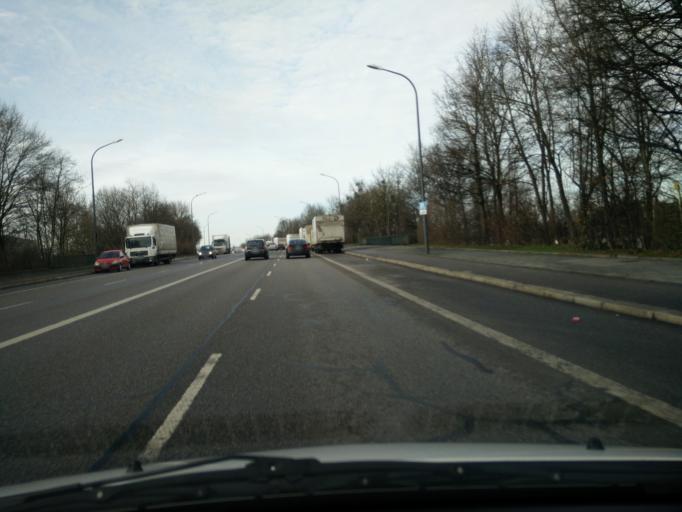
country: DE
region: Bavaria
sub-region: Upper Bavaria
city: Karlsfeld
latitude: 48.1737
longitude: 11.5032
